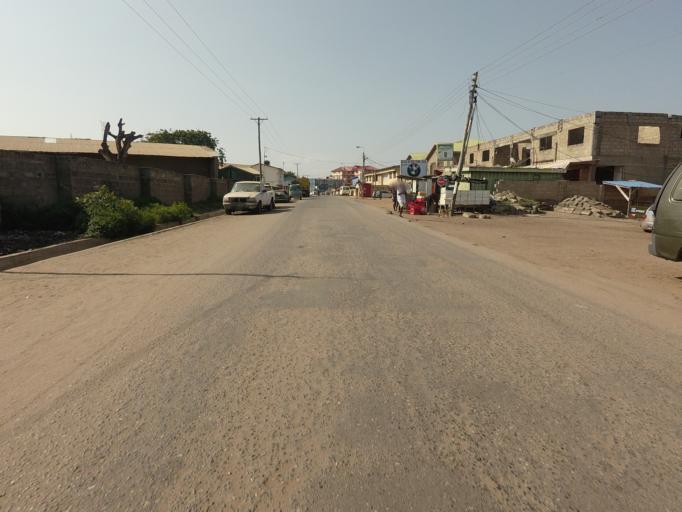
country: GH
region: Greater Accra
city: Teshi Old Town
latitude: 5.5846
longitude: -0.1012
